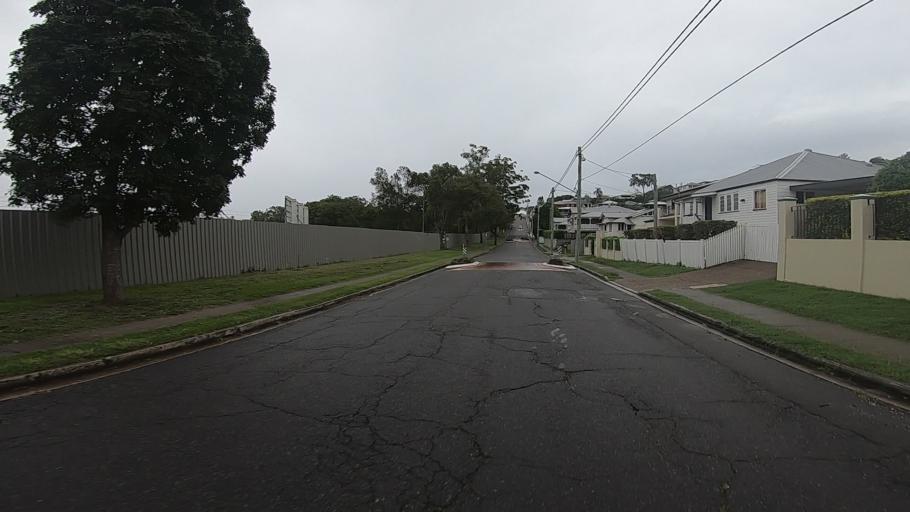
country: AU
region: Queensland
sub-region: Brisbane
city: Ascot
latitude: -27.4383
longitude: 153.0491
